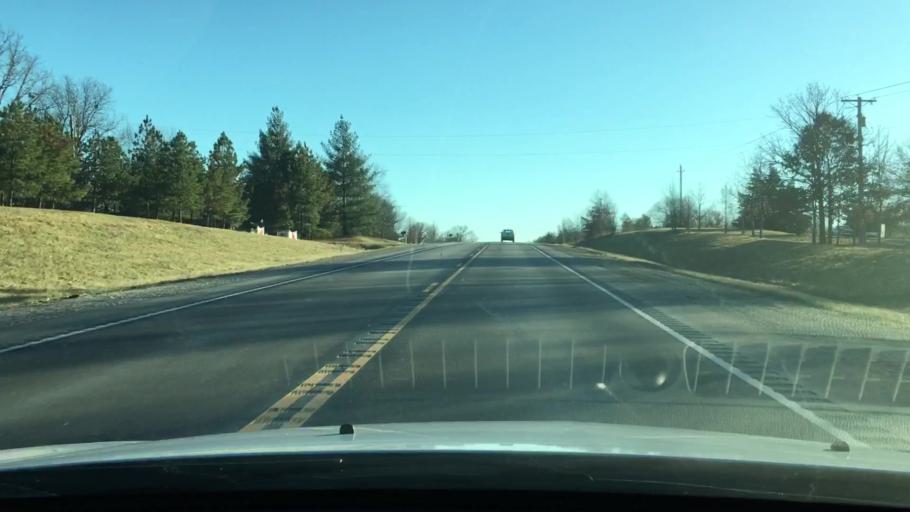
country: US
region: Missouri
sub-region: Boone County
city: Centralia
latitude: 39.1724
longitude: -92.1776
